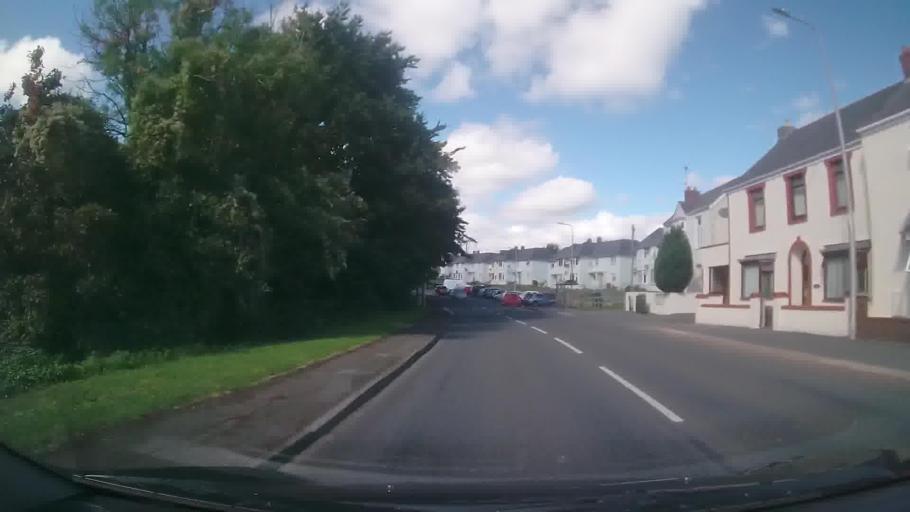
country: GB
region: Wales
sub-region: Pembrokeshire
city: Tenby
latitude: 51.6723
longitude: -4.7159
